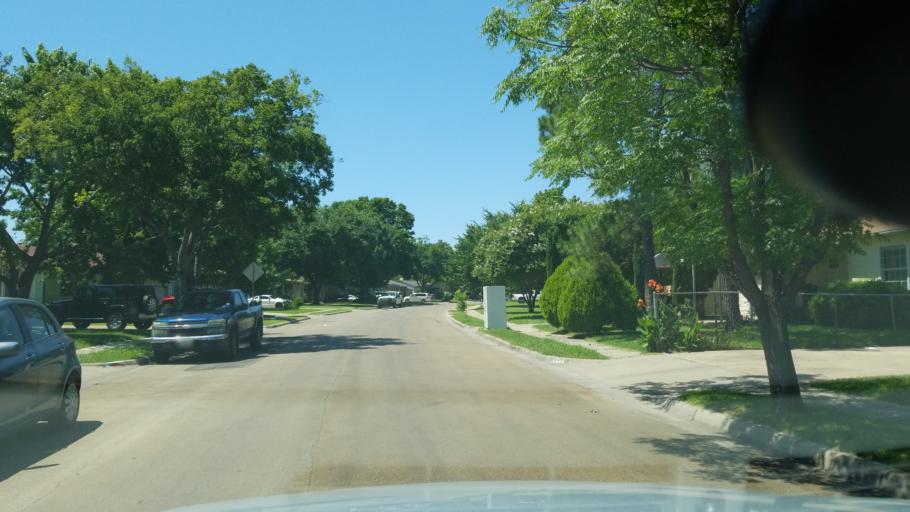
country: US
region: Texas
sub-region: Dallas County
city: Irving
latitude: 32.8320
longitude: -96.9339
